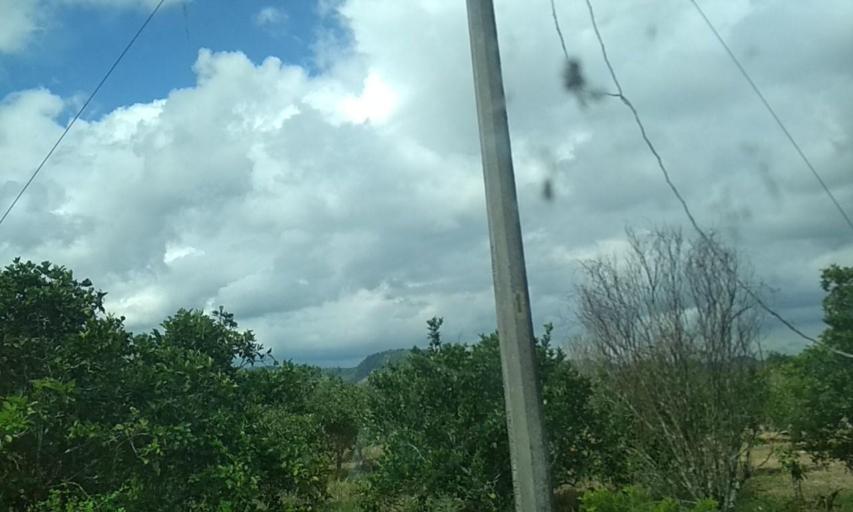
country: MX
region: Puebla
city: San Jose Acateno
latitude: 20.2781
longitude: -97.1318
